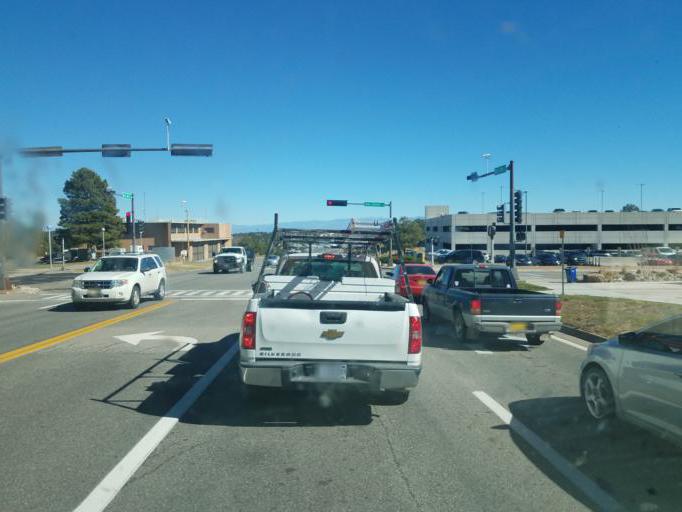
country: US
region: New Mexico
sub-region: Los Alamos County
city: Los Alamos
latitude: 35.8768
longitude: -106.3253
